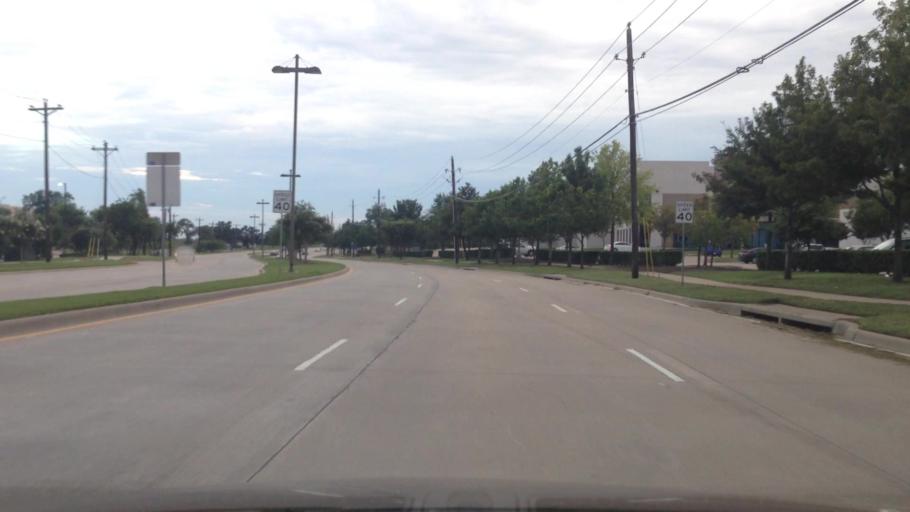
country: US
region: Texas
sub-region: Denton County
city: Flower Mound
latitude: 32.9985
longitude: -97.0464
